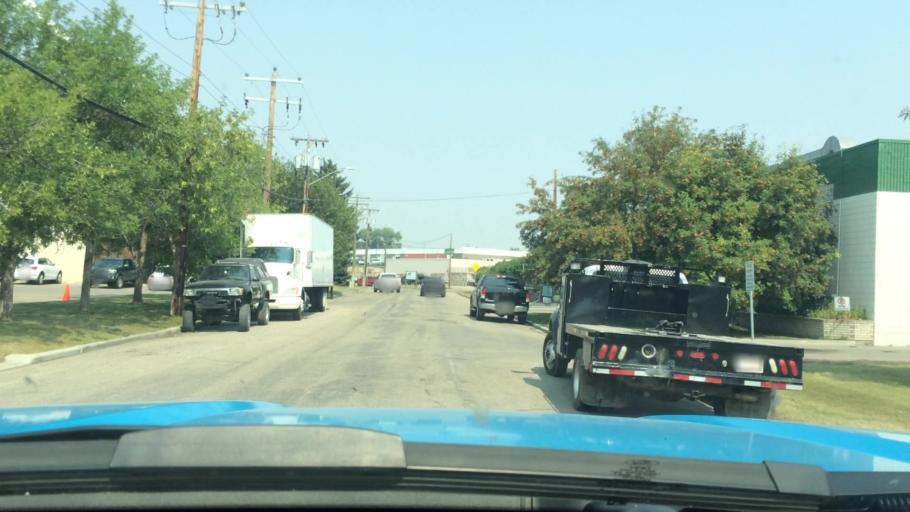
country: CA
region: Alberta
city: Calgary
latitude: 51.0128
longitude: -114.0560
